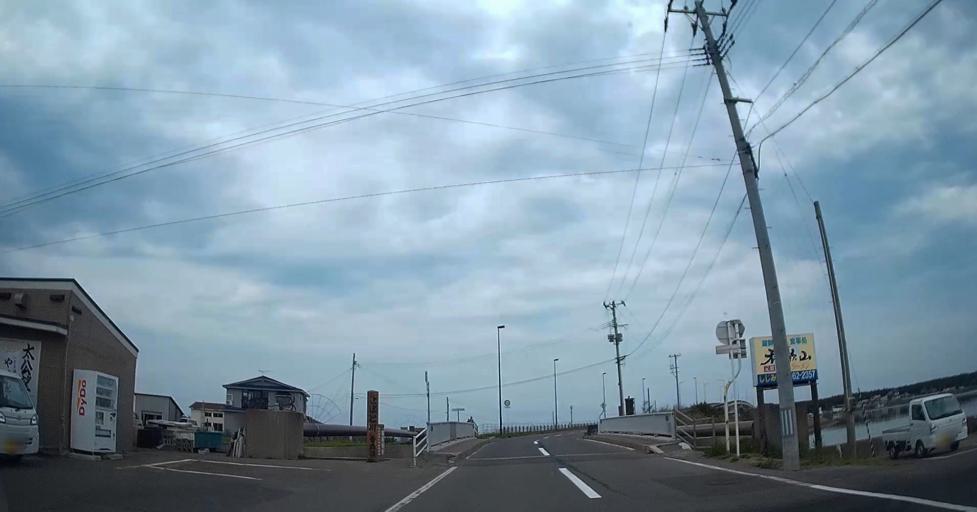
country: JP
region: Aomori
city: Shimokizukuri
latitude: 41.0368
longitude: 140.3288
